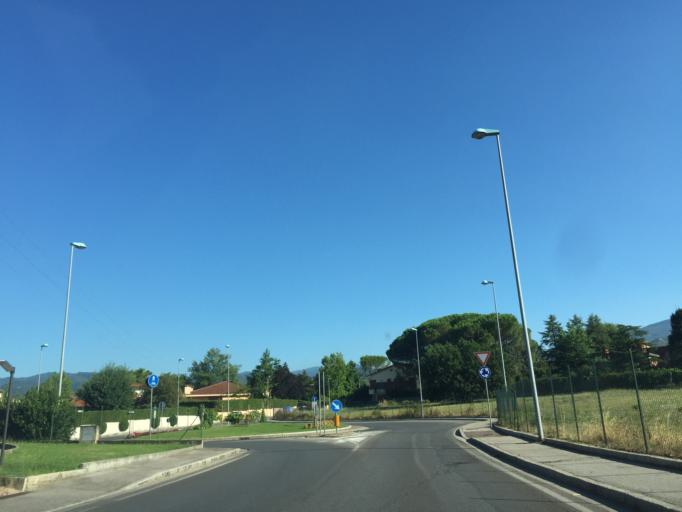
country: IT
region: Tuscany
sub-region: Provincia di Pistoia
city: Pistoia
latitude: 43.9433
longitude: 10.9246
